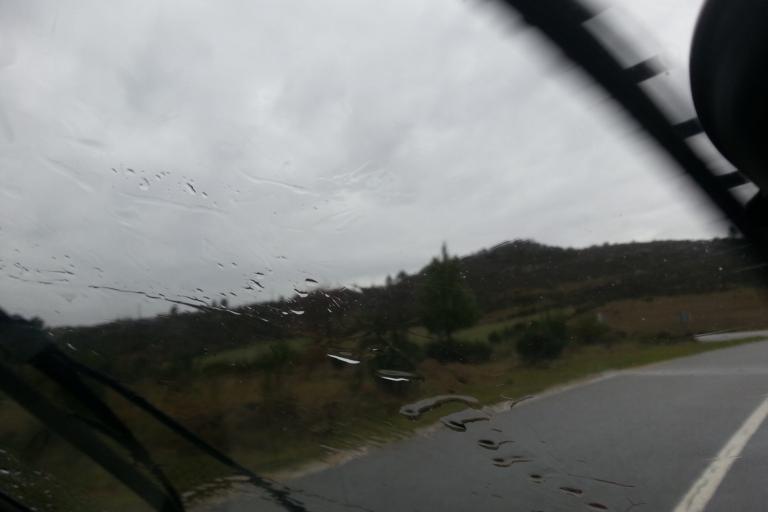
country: PT
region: Guarda
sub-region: Fornos de Algodres
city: Fornos de Algodres
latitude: 40.5785
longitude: -7.5116
